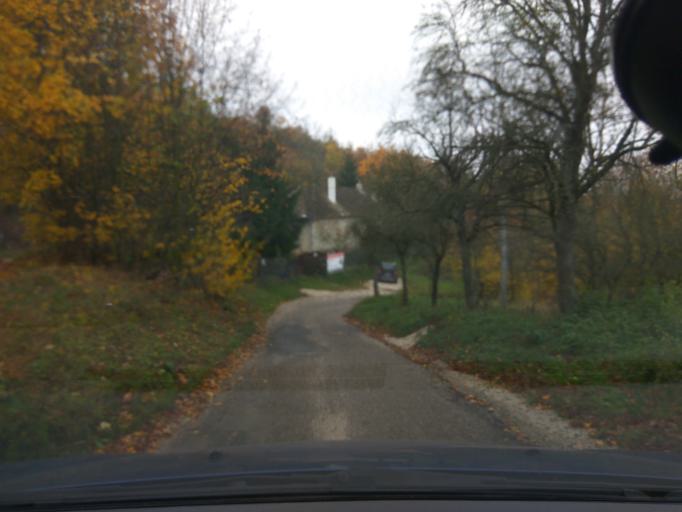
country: SK
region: Trnavsky
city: Vrbove
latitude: 48.6841
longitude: 17.7004
